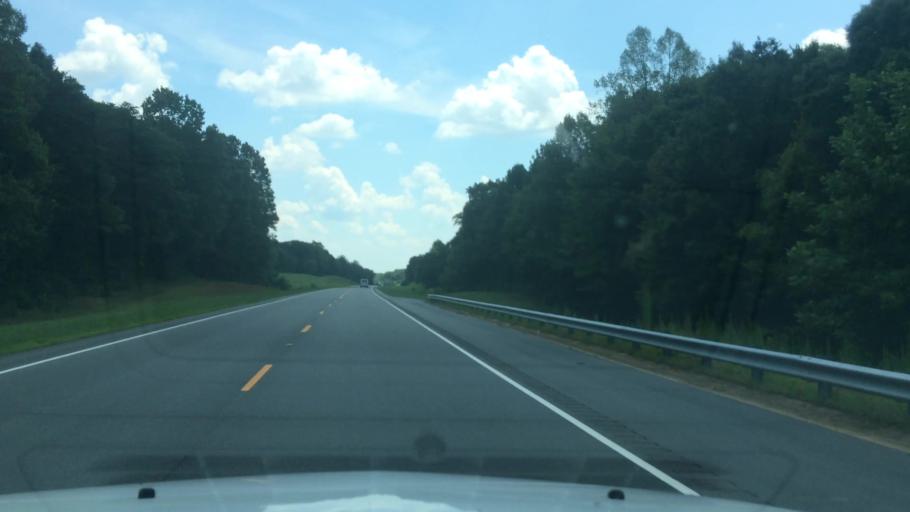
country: US
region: North Carolina
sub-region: Alexander County
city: Stony Point
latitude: 35.8740
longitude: -81.0671
